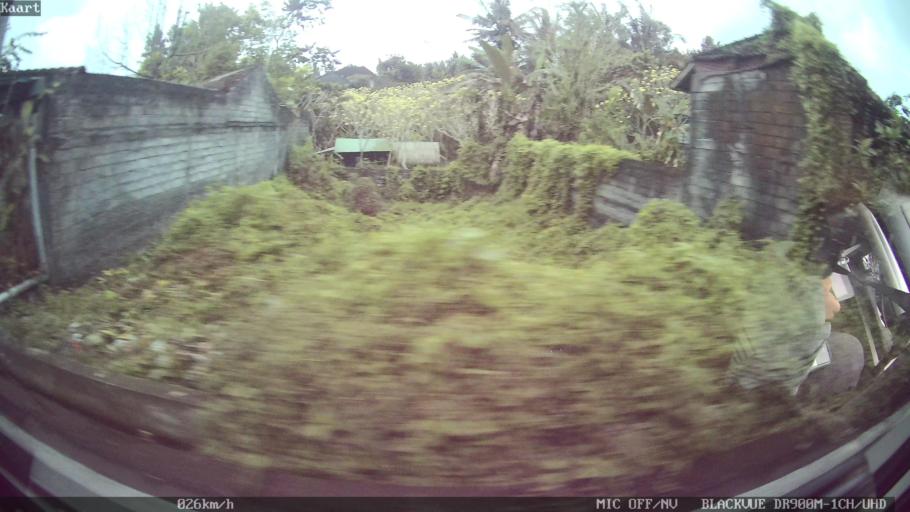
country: ID
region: Bali
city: Banjar Mambalkajanan
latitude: -8.5608
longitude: 115.2140
